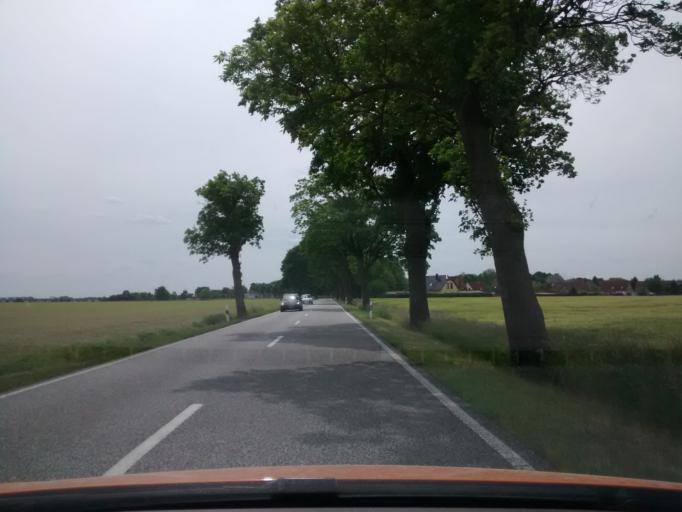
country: DE
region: Brandenburg
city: Juterbog
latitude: 51.9367
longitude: 13.1205
